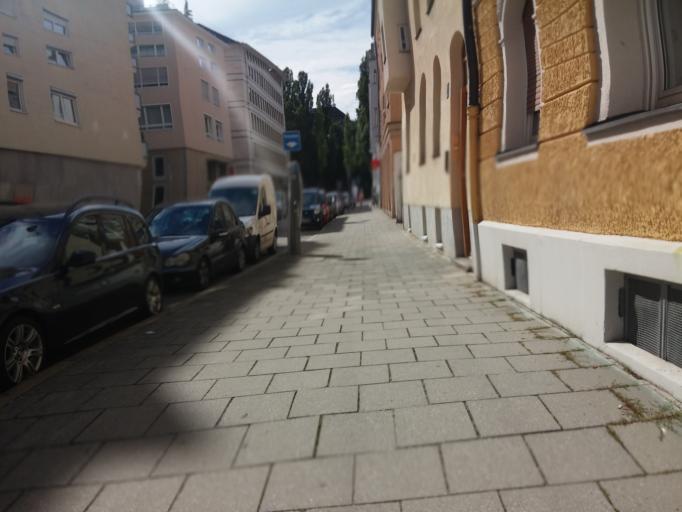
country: DE
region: Bavaria
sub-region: Upper Bavaria
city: Munich
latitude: 48.1540
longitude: 11.5849
